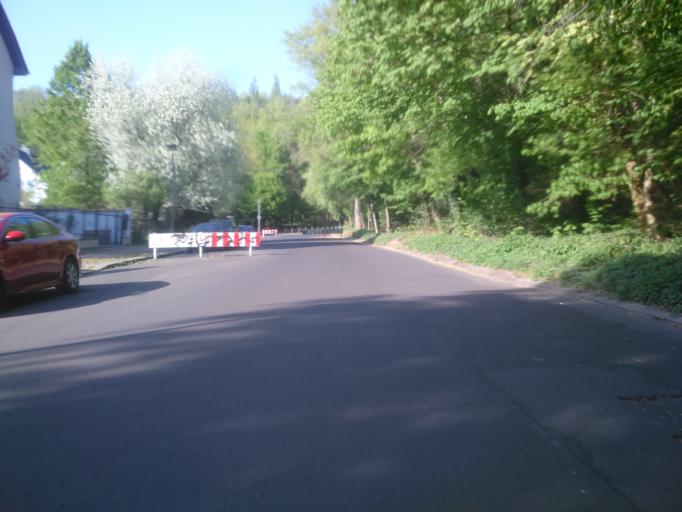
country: DE
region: Berlin
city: Fennpfuhl
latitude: 52.5344
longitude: 13.4615
